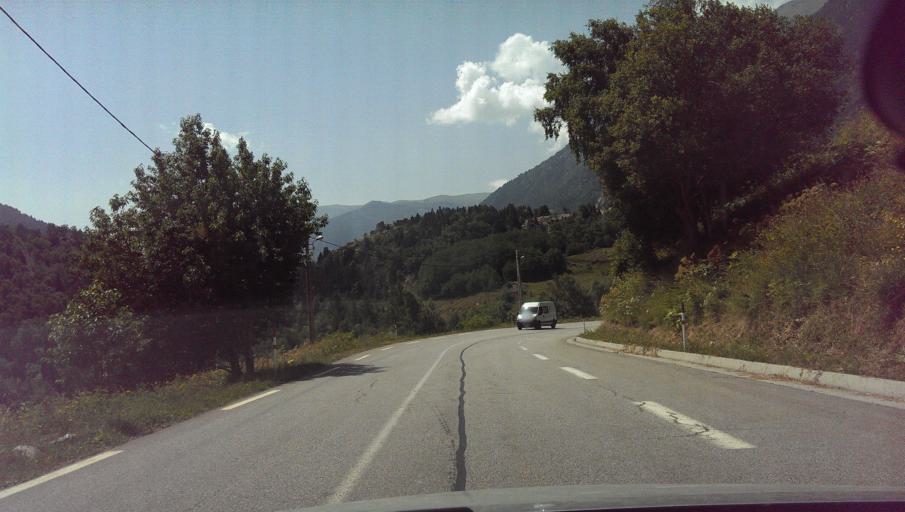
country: AD
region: Encamp
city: Pas de la Casa
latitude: 42.5481
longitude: 1.8270
